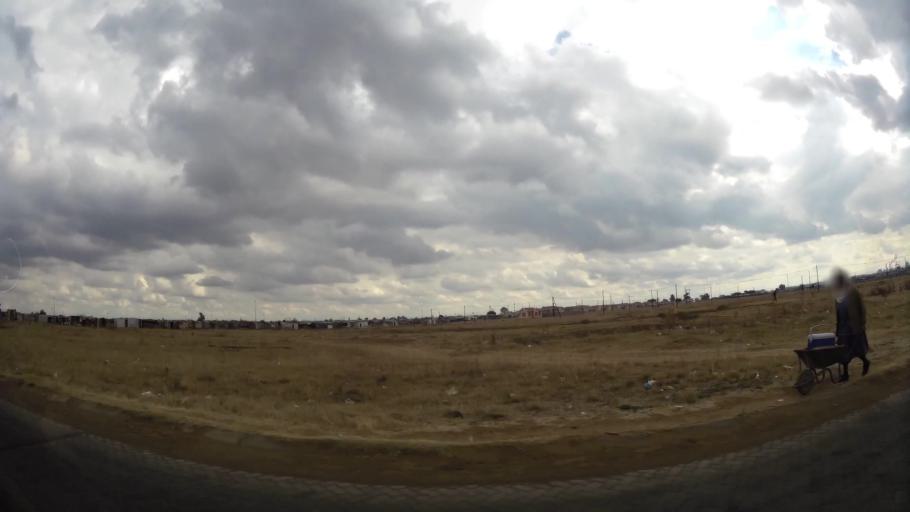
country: ZA
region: Orange Free State
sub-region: Fezile Dabi District Municipality
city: Sasolburg
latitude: -26.8591
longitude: 27.8724
